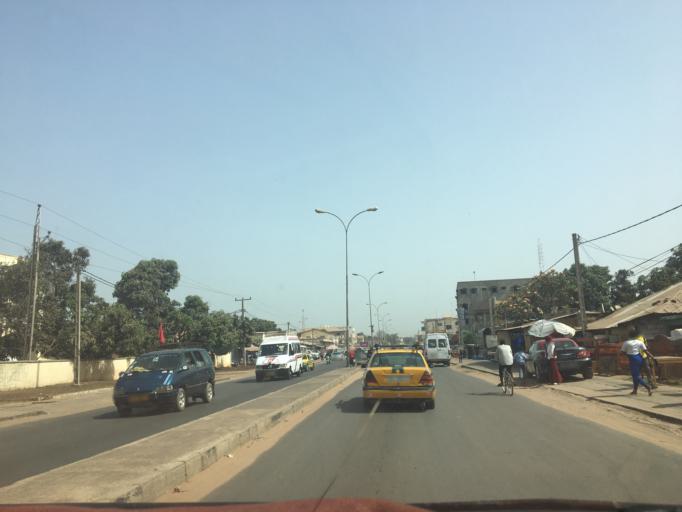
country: GM
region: Western
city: Abuko
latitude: 13.4340
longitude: -16.6758
